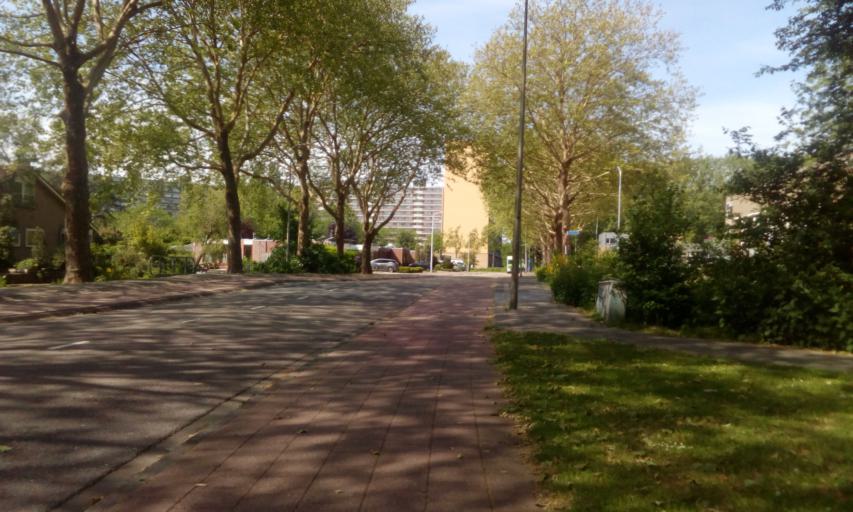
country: NL
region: South Holland
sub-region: Gemeente Capelle aan den IJssel
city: Capelle aan den IJssel
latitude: 51.9264
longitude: 4.5759
